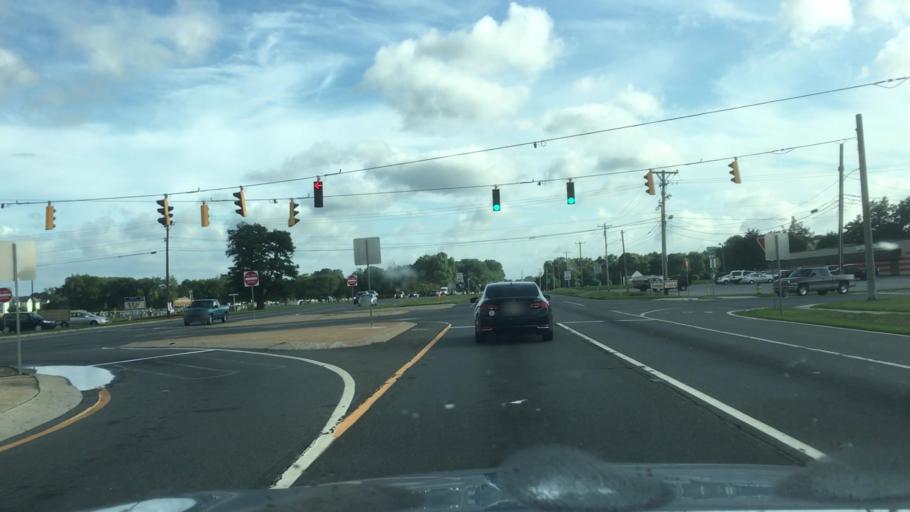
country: US
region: Delaware
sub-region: Sussex County
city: Milford
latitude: 38.9280
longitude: -75.4328
